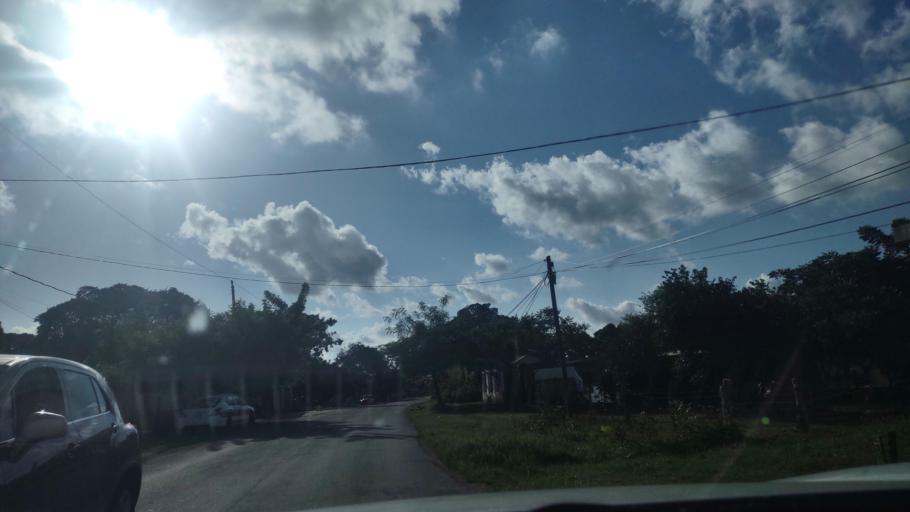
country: MX
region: Veracruz
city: El Tejar
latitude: 19.0706
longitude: -96.1680
